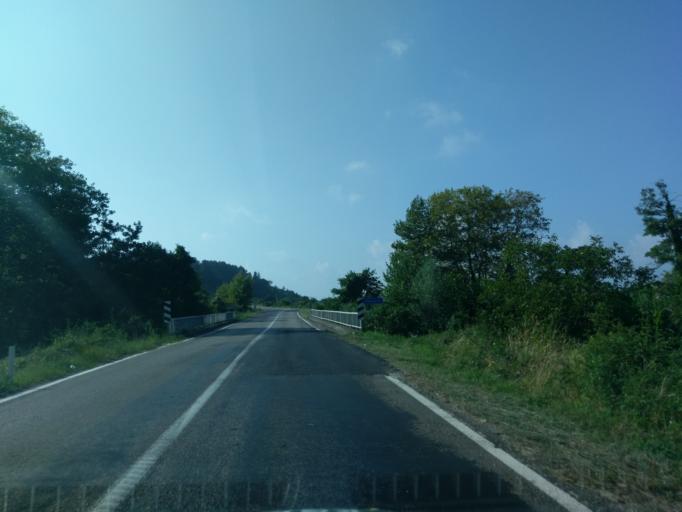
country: TR
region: Sinop
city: Yenikonak
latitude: 41.9401
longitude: 34.7202
